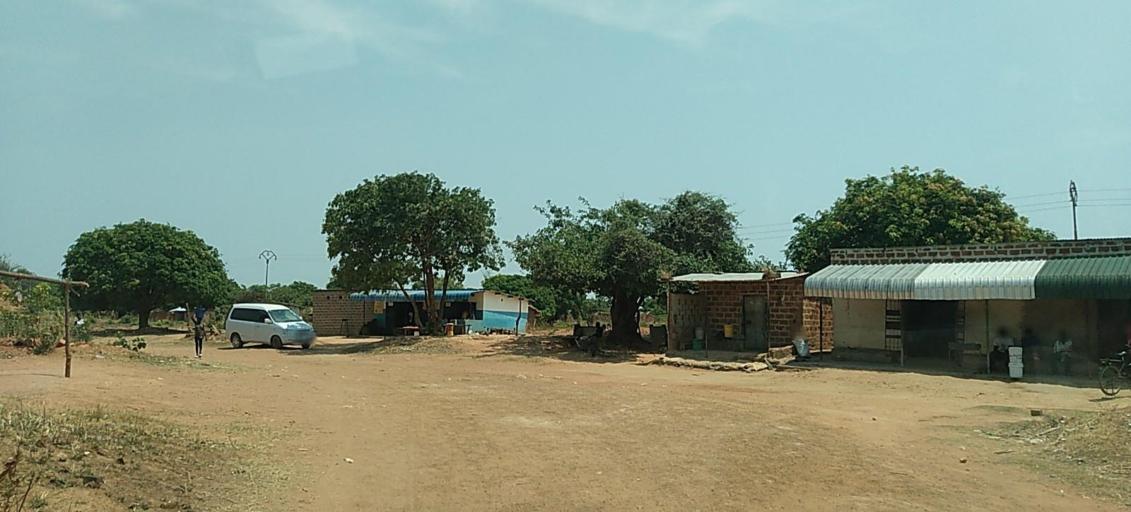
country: ZM
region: Copperbelt
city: Ndola
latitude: -13.0735
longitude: 28.7465
